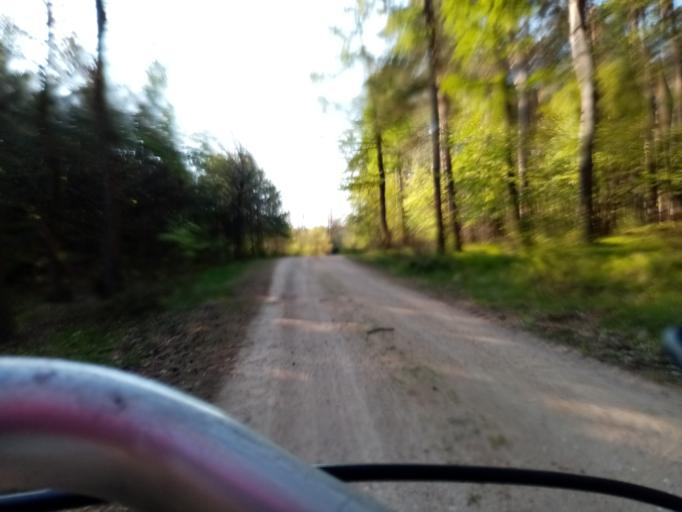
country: PL
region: Kujawsko-Pomorskie
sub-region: Powiat brodnicki
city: Gorzno
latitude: 53.1680
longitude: 19.6731
